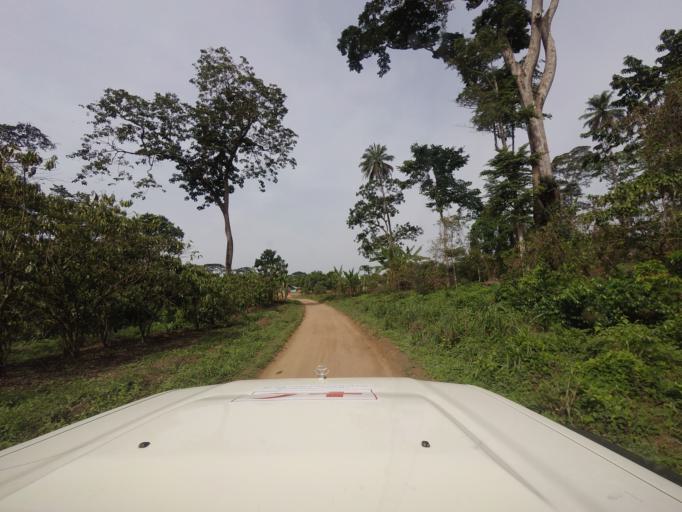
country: GN
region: Nzerekore
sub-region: Macenta
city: Macenta
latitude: 8.4821
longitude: -9.5474
